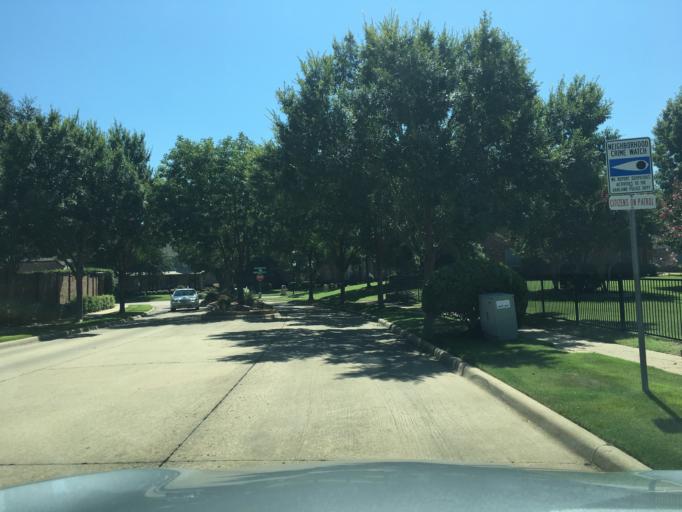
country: US
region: Texas
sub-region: Dallas County
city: Sachse
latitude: 32.9601
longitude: -96.6247
